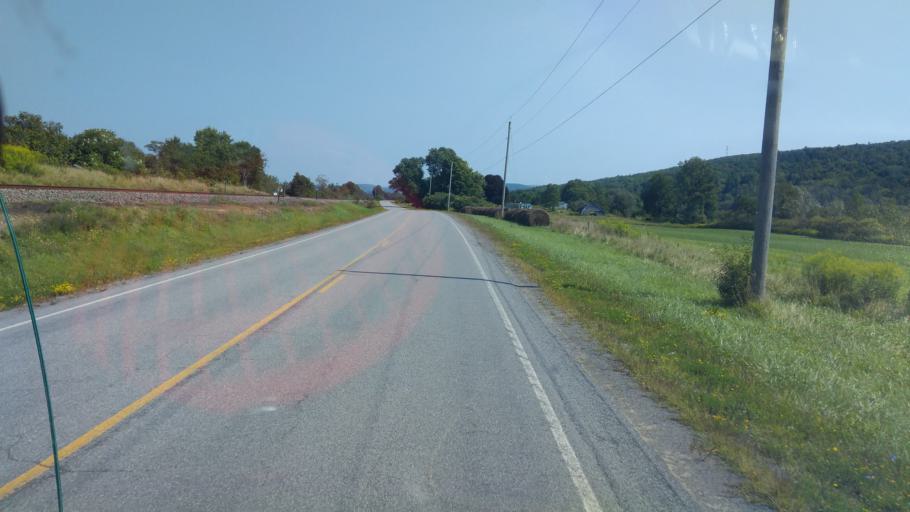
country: US
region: New York
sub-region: Allegany County
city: Belmont
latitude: 42.2328
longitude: -78.0854
